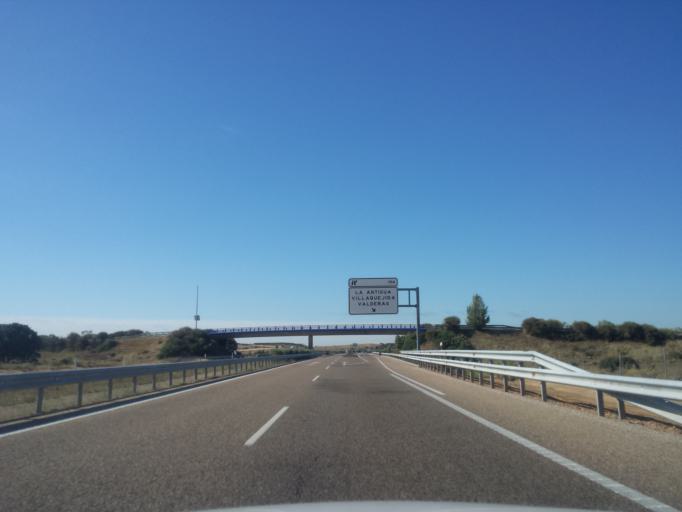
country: ES
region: Castille and Leon
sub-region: Provincia de Leon
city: Villaquejida
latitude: 42.1575
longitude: -5.6361
